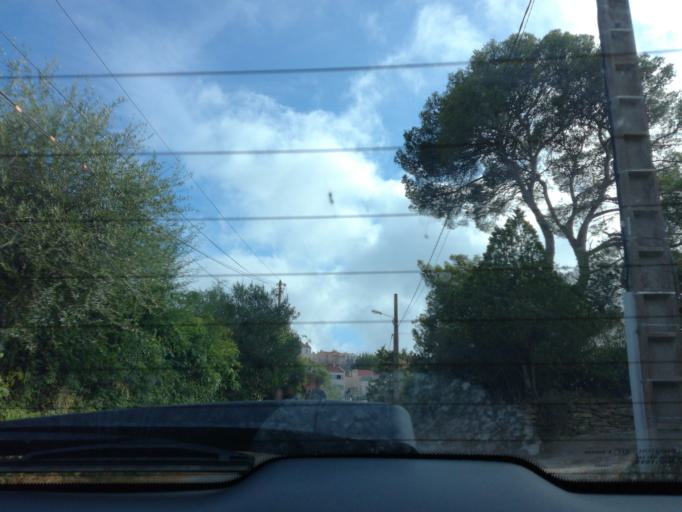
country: FR
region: Provence-Alpes-Cote d'Azur
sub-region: Departement du Var
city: Hyeres
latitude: 43.0404
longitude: 6.1321
